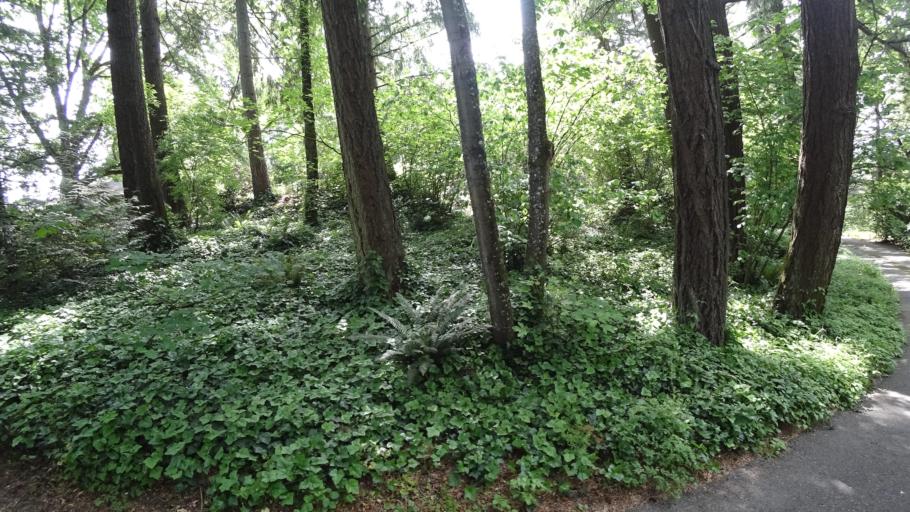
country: US
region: Oregon
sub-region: Clackamas County
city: Lake Oswego
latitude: 45.4425
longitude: -122.6694
